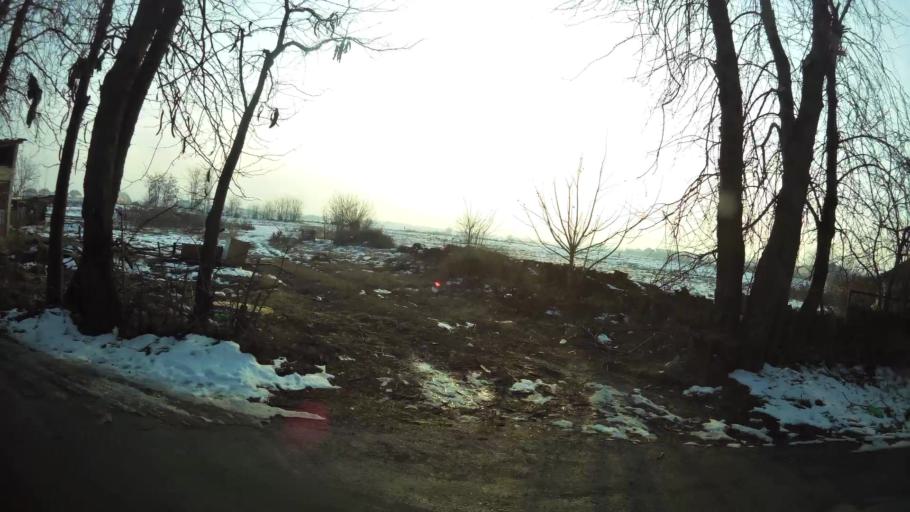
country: MK
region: Aracinovo
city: Arachinovo
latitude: 42.0134
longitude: 21.5259
